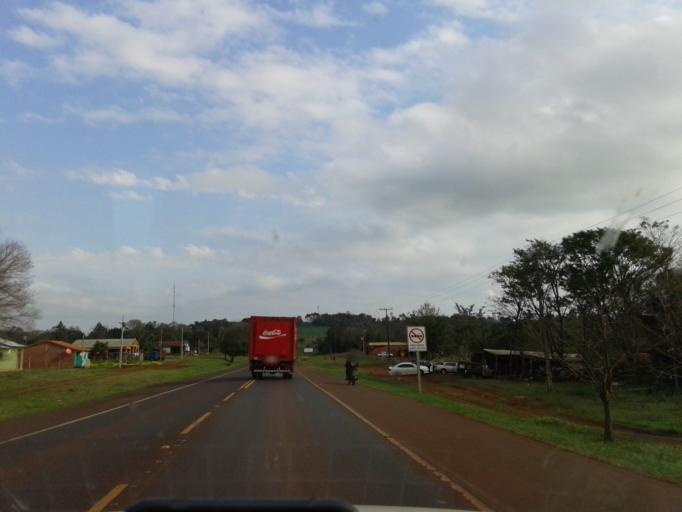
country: PY
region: Itapua
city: Edelira
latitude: -26.7141
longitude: -55.3293
